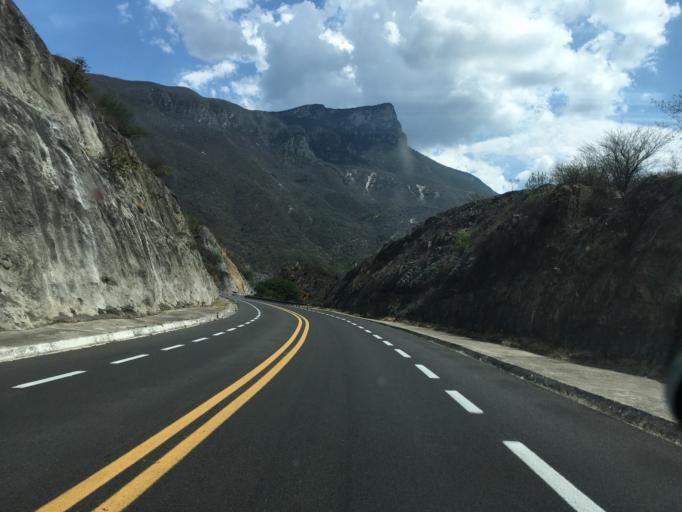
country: MX
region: Puebla
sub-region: San Jose Miahuatlan
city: San Pedro Tetitlan
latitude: 18.1515
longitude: -97.3061
